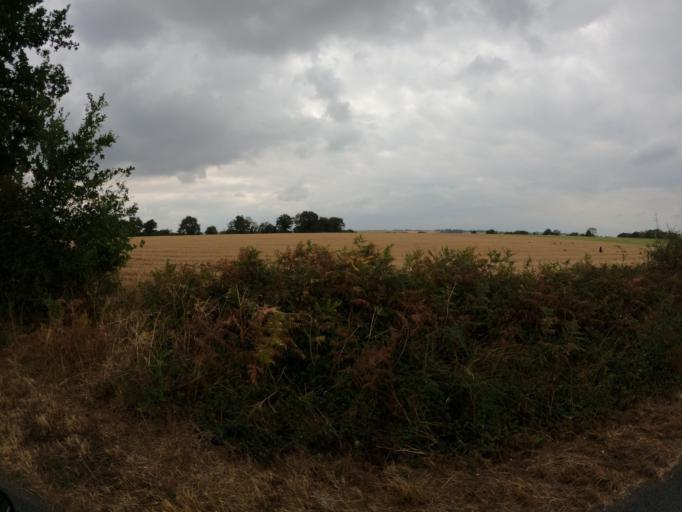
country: FR
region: Pays de la Loire
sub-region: Departement de Maine-et-Loire
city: Le Longeron
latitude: 47.0052
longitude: -1.0665
